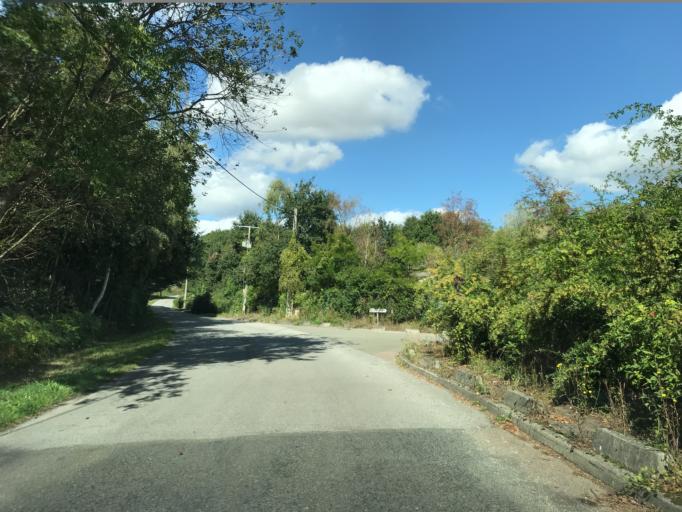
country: FR
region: Haute-Normandie
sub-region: Departement de l'Eure
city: La Chapelle-Reanville
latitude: 49.0899
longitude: 1.3960
